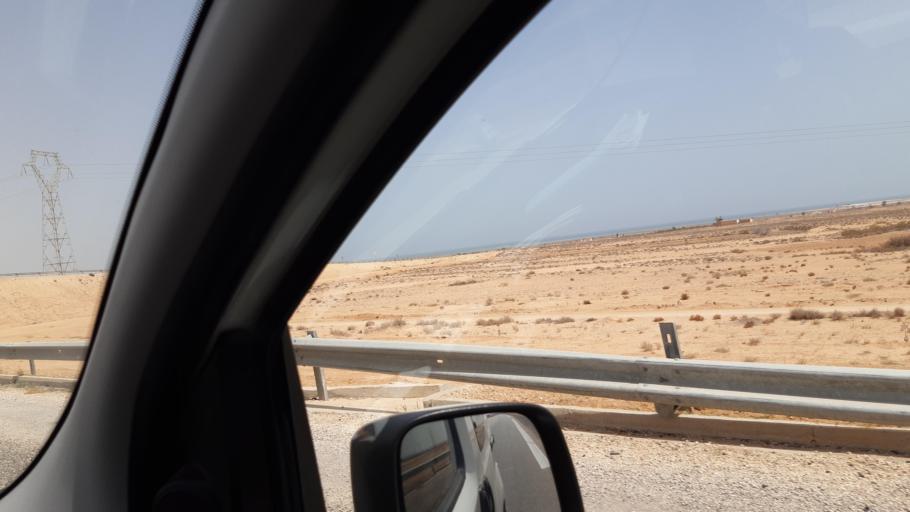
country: TN
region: Safaqis
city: Skhira
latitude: 34.1547
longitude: 9.9699
